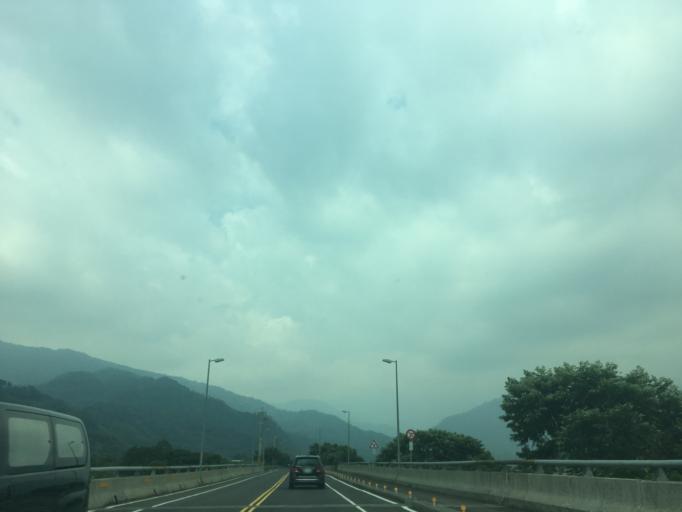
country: TW
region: Taiwan
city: Fengyuan
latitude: 24.2952
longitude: 120.8734
